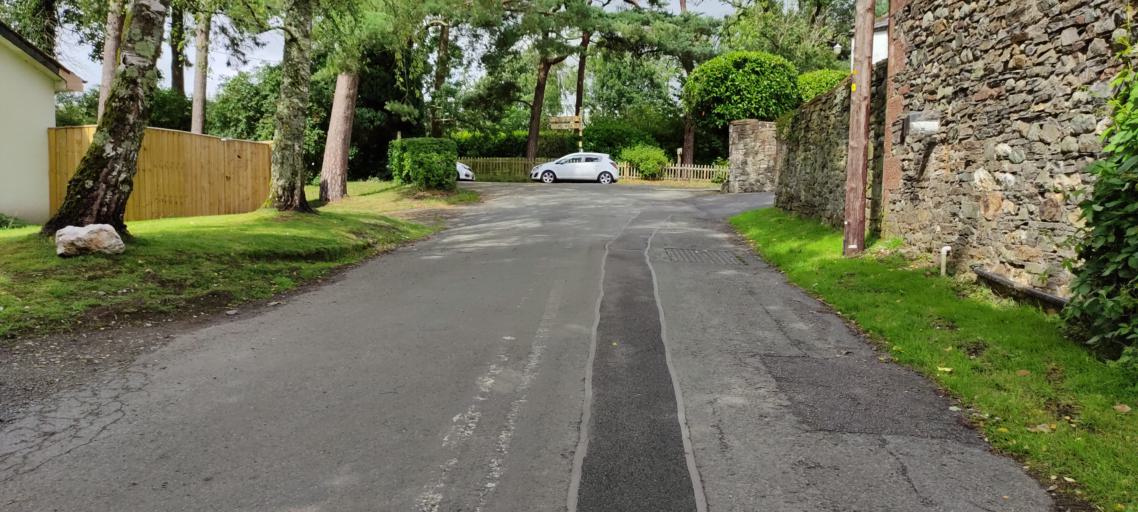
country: GB
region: England
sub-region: Cumbria
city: Cockermouth
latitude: 54.6650
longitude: -3.2426
